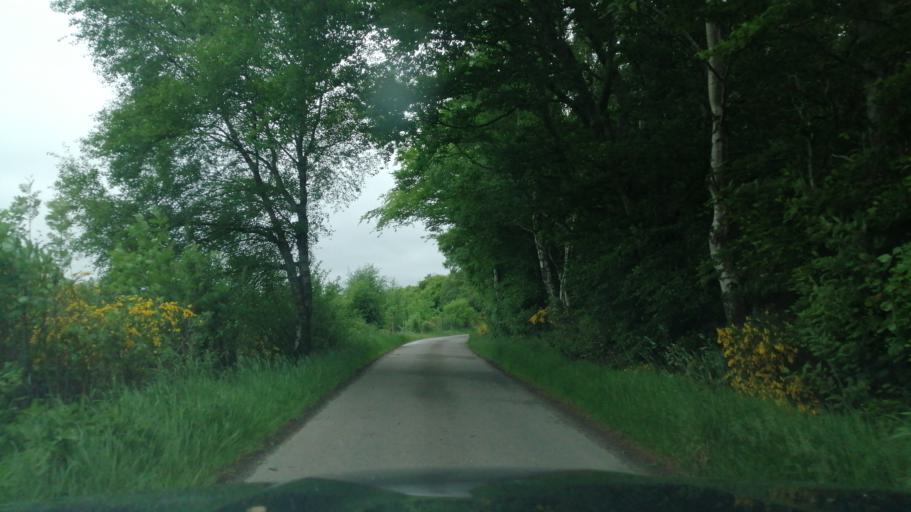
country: GB
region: Scotland
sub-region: Moray
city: Keith
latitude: 57.5615
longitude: -2.8621
